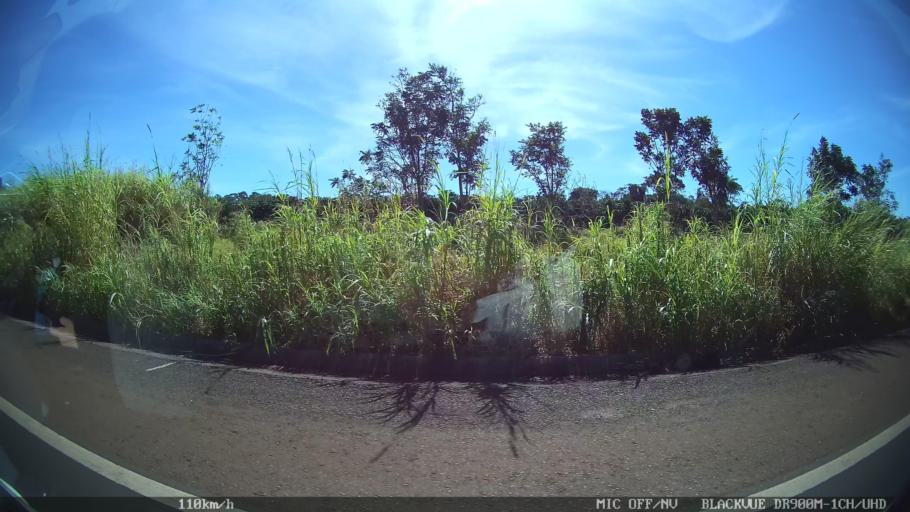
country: BR
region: Sao Paulo
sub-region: Franca
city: Franca
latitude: -20.5558
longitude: -47.5867
